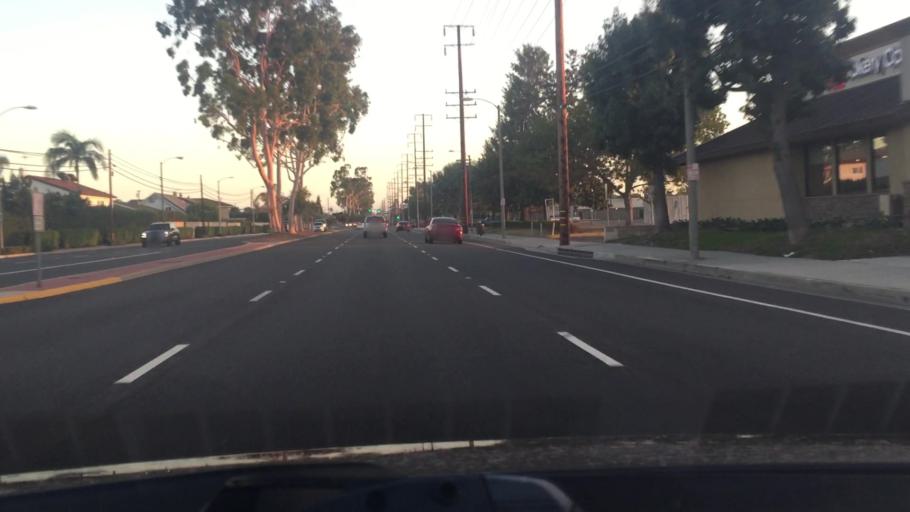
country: US
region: California
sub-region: Orange County
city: Cypress
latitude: 33.8229
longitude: -118.0284
